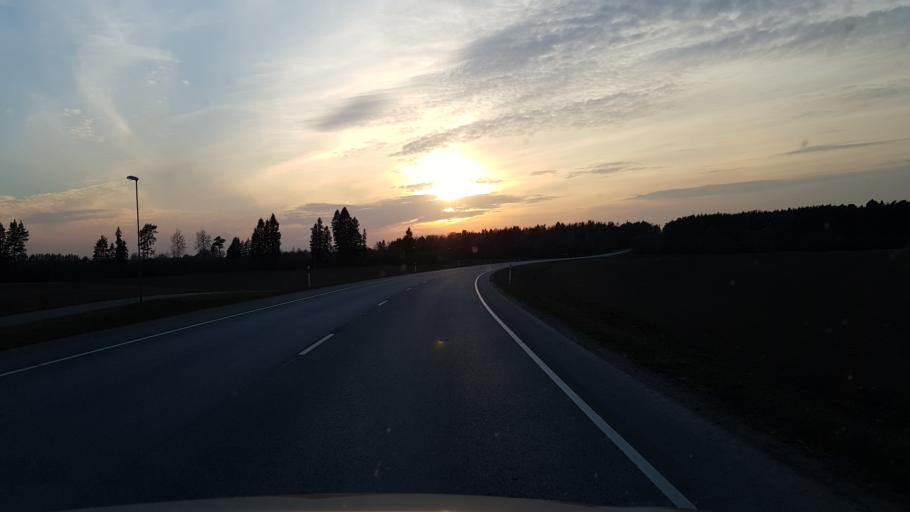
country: EE
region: Laeaene-Virumaa
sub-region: Rakvere linn
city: Rakvere
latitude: 59.3208
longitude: 26.3651
